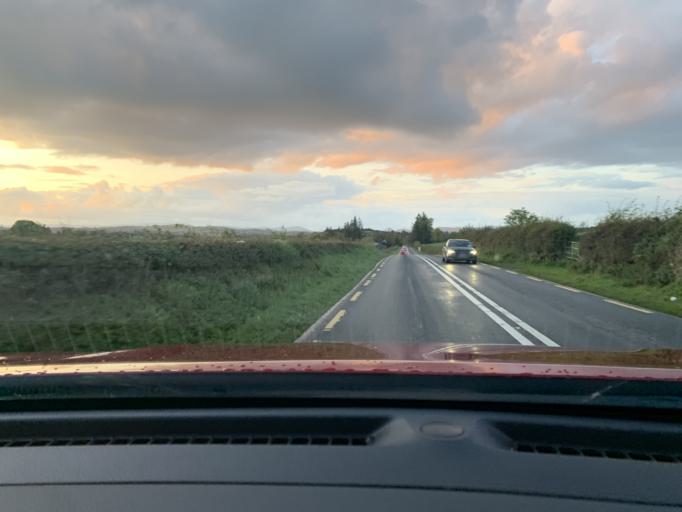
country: IE
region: Connaught
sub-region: Sligo
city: Ballymote
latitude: 54.1170
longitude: -8.4271
